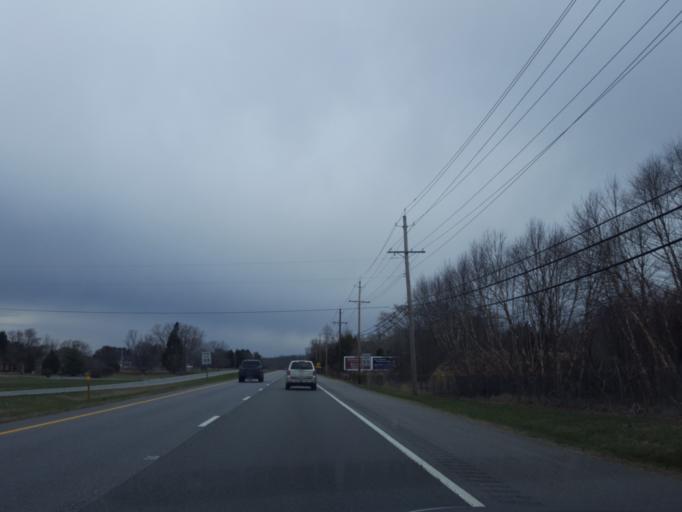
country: US
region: Maryland
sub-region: Calvert County
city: Dunkirk
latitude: 38.7371
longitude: -76.6591
